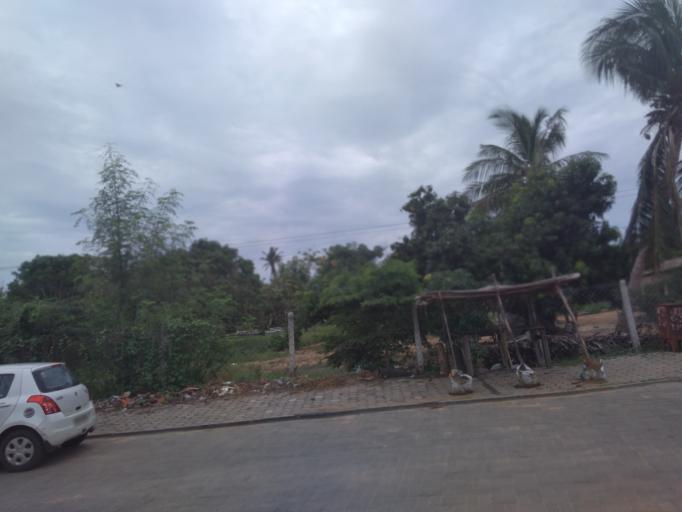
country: IN
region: Tamil Nadu
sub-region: Kancheepuram
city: Injambakkam
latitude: 12.8678
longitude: 80.2264
